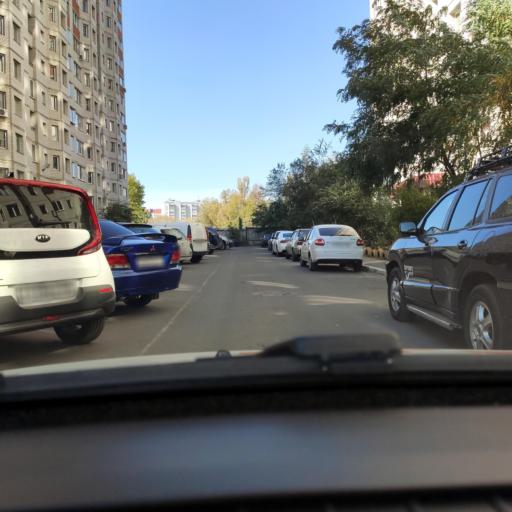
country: RU
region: Voronezj
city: Voronezh
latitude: 51.6437
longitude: 39.1631
